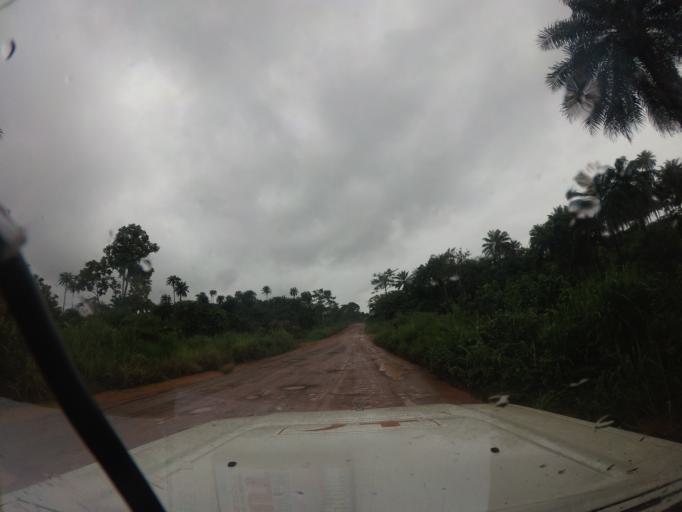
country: SL
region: Eastern Province
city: Tefeya
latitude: 8.5699
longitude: -11.2913
